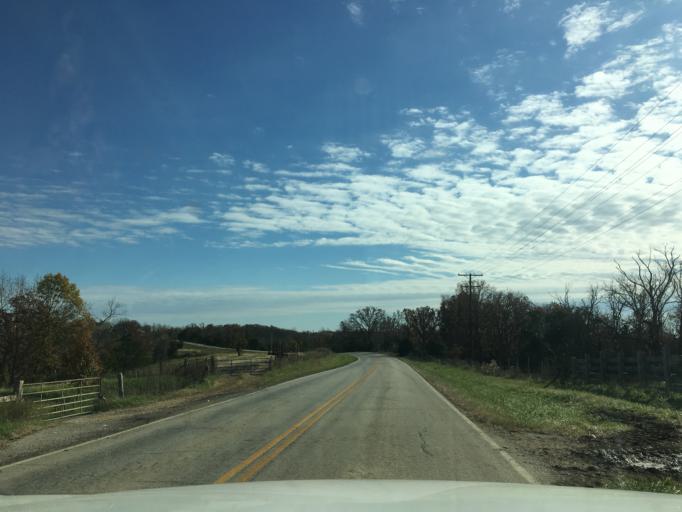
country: US
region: Missouri
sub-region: Osage County
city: Linn
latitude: 38.4401
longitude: -91.8351
